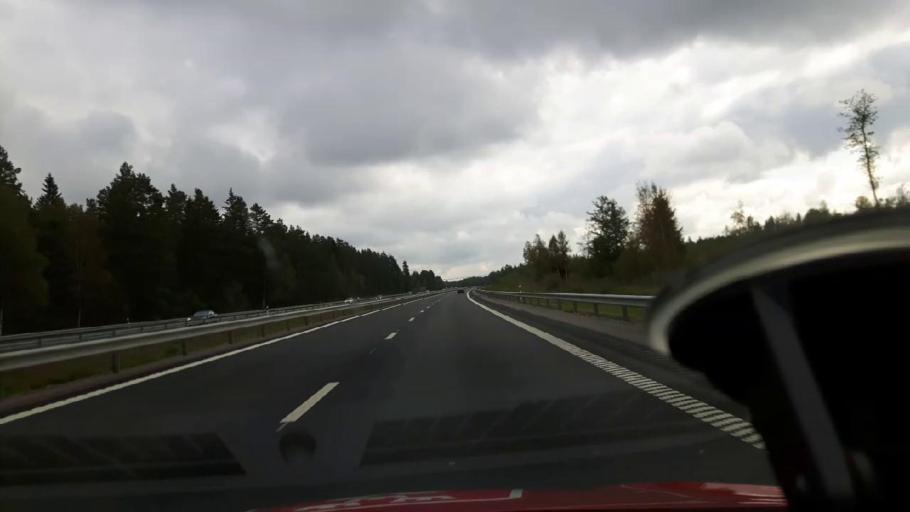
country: SE
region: Gaevleborg
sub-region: Gavle Kommun
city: Gavle
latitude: 60.6324
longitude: 17.1486
